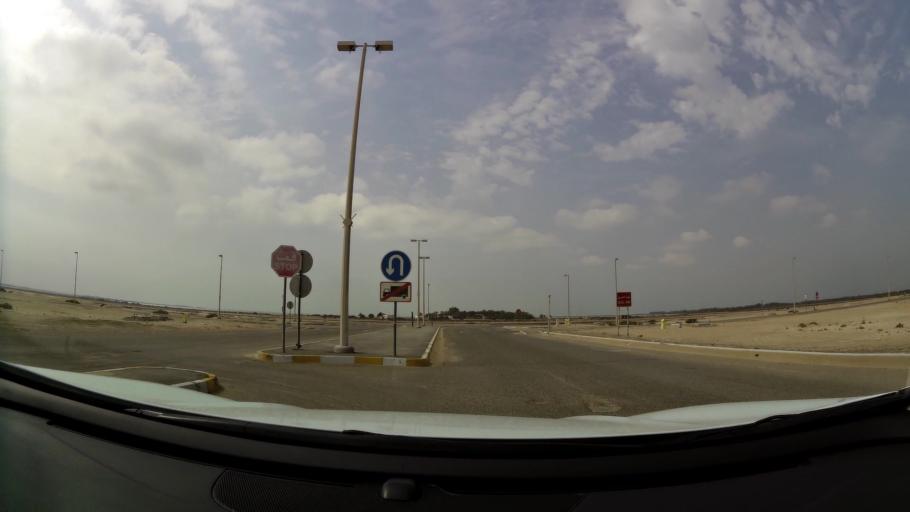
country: AE
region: Abu Dhabi
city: Abu Dhabi
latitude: 24.6060
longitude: 54.6442
